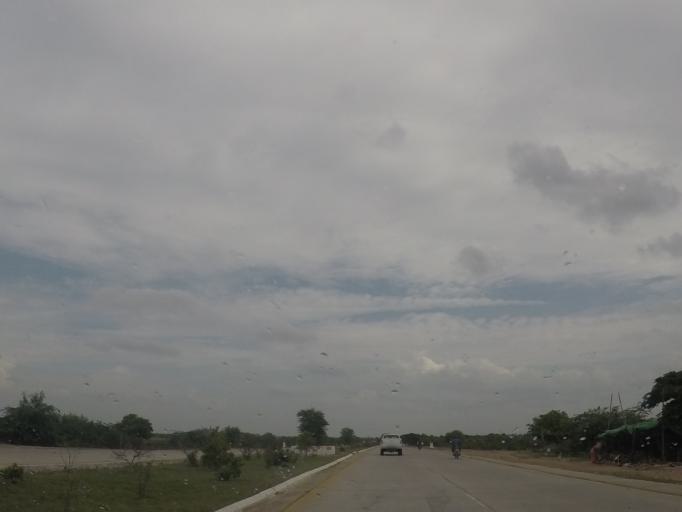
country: MM
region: Sagain
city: Sagaing
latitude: 21.7840
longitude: 95.9691
